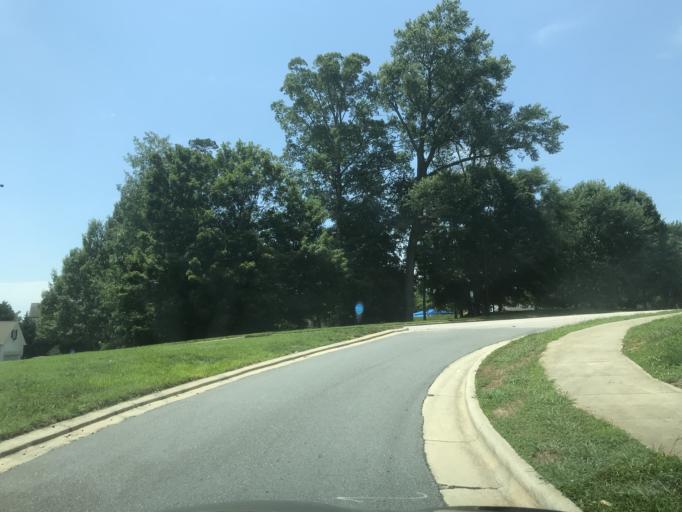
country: US
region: North Carolina
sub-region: Wake County
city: Wake Forest
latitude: 35.9392
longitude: -78.5616
